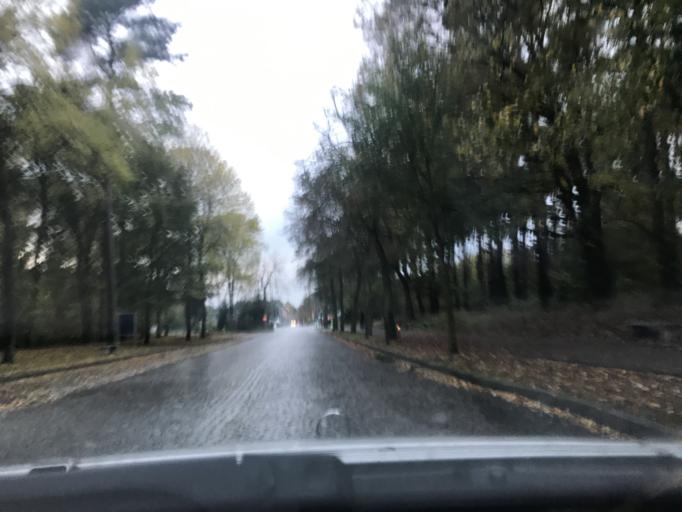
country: PL
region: West Pomeranian Voivodeship
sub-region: Swinoujscie
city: Swinoujscie
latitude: 53.9209
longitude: 14.2197
